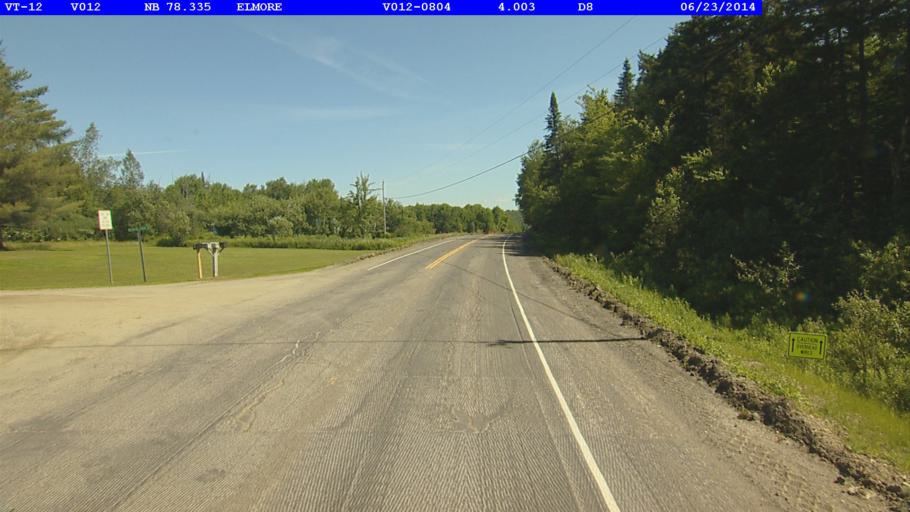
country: US
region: Vermont
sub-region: Lamoille County
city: Morrisville
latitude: 44.5030
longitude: -72.5167
